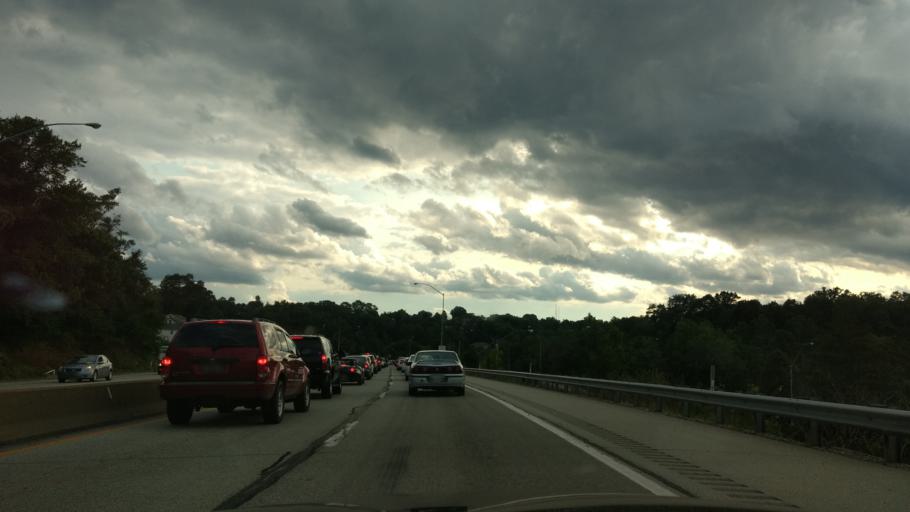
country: US
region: Pennsylvania
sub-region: Allegheny County
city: Swissvale
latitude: 40.4286
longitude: -79.8893
